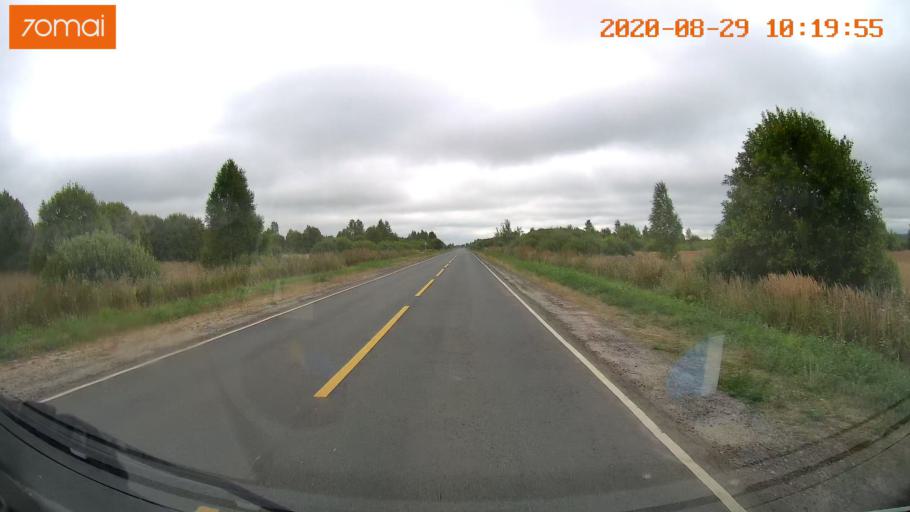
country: RU
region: Ivanovo
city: Yur'yevets
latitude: 57.3259
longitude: 42.8714
